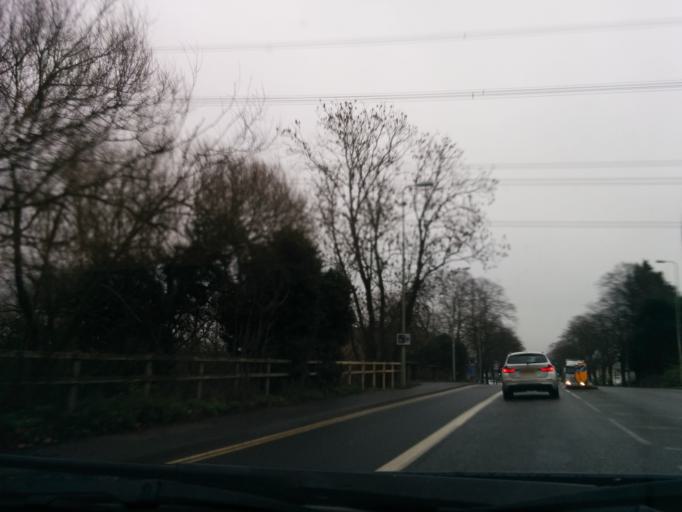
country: GB
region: England
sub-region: Oxfordshire
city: Oxford
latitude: 51.7534
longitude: -1.2913
